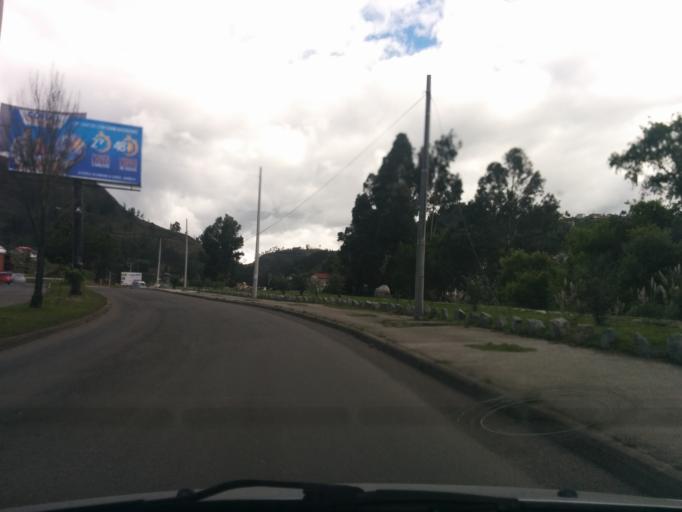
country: EC
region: Azuay
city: Cuenca
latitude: -2.9209
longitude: -79.0280
